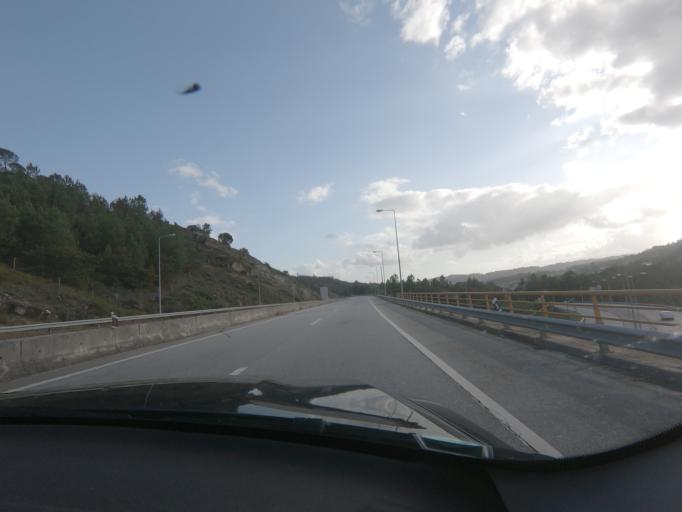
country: PT
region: Viseu
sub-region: Viseu
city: Viseu
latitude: 40.6124
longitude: -7.9653
